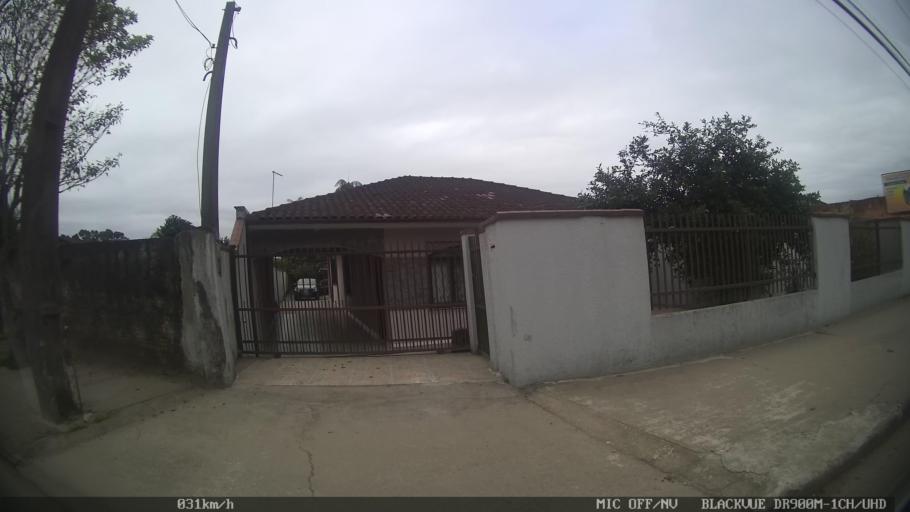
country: BR
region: Santa Catarina
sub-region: Joinville
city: Joinville
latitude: -26.2676
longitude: -48.8906
